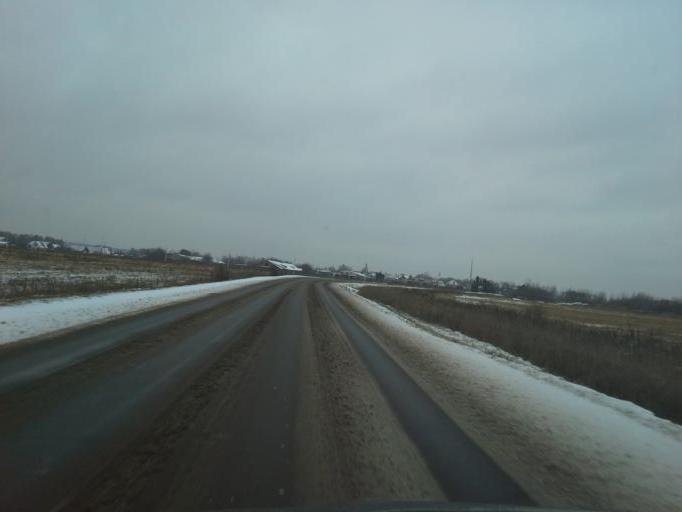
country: RU
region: Moskovskaya
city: Gorki Vtoryye
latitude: 55.7367
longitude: 37.1107
